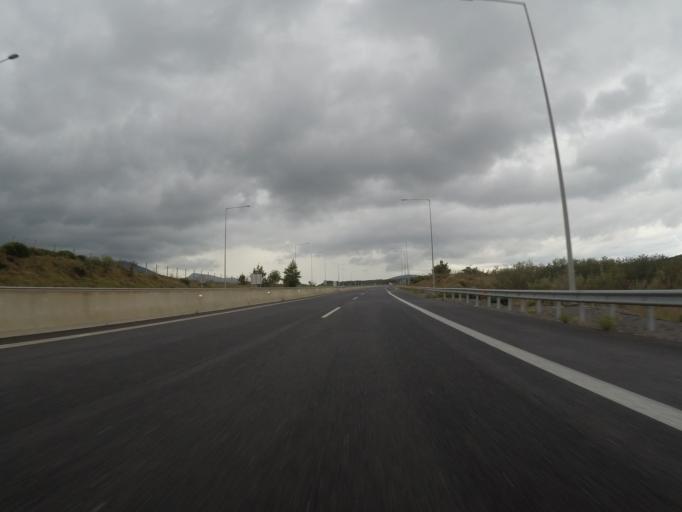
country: GR
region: Peloponnese
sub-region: Nomos Arkadias
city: Megalopoli
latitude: 37.3444
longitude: 22.1094
